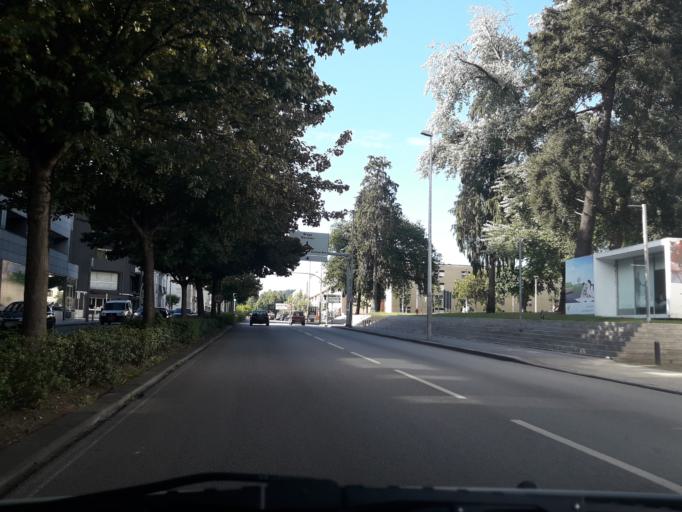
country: PT
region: Braga
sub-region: Vila Nova de Famalicao
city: Vila Nova de Famalicao
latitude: 41.4058
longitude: -8.5164
